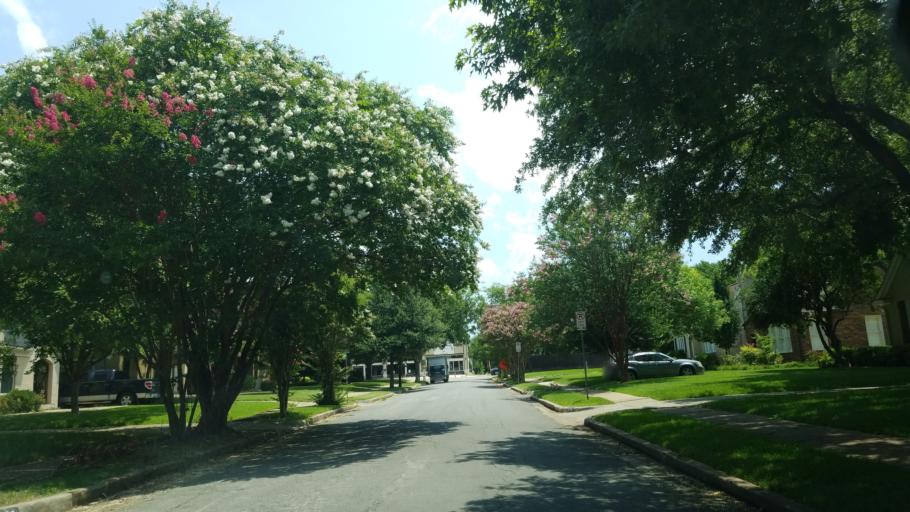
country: US
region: Texas
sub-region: Dallas County
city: Highland Park
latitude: 32.8255
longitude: -96.7713
